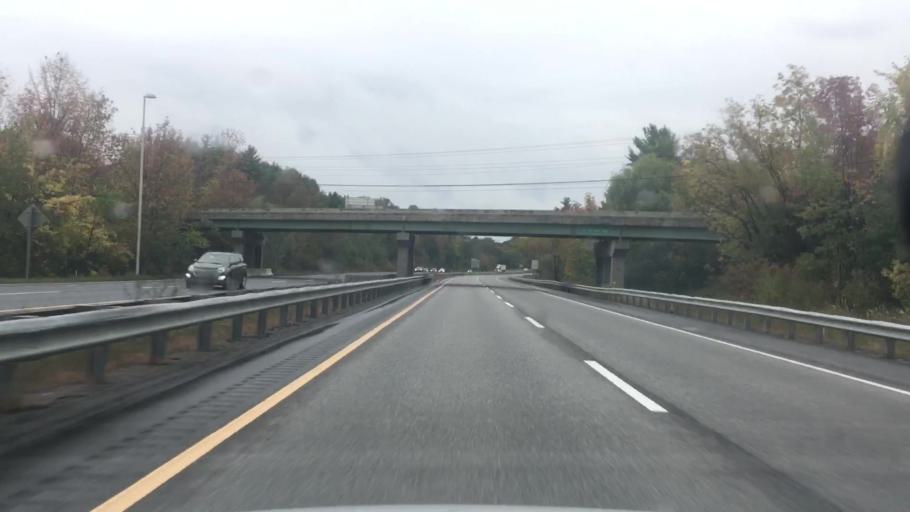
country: US
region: Maine
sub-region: Kennebec County
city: Augusta
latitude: 44.3196
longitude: -69.8131
